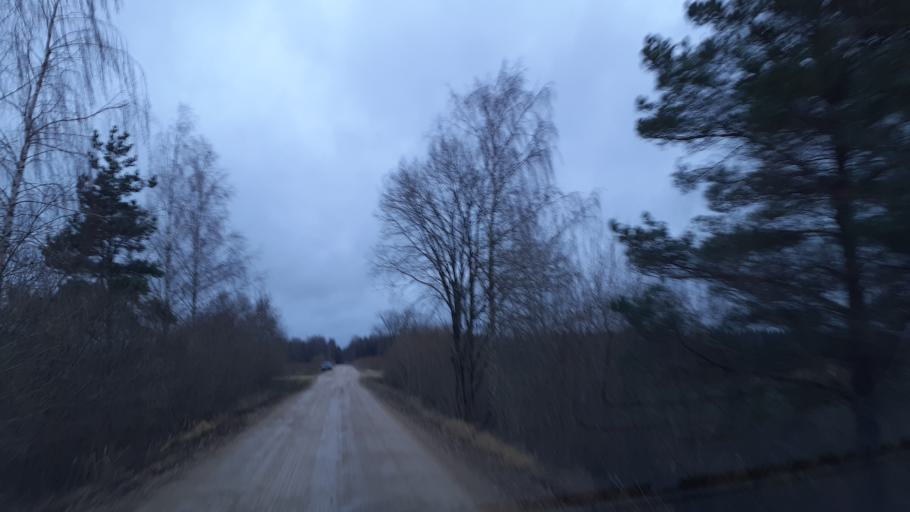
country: LV
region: Kuldigas Rajons
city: Kuldiga
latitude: 57.0453
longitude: 22.1330
